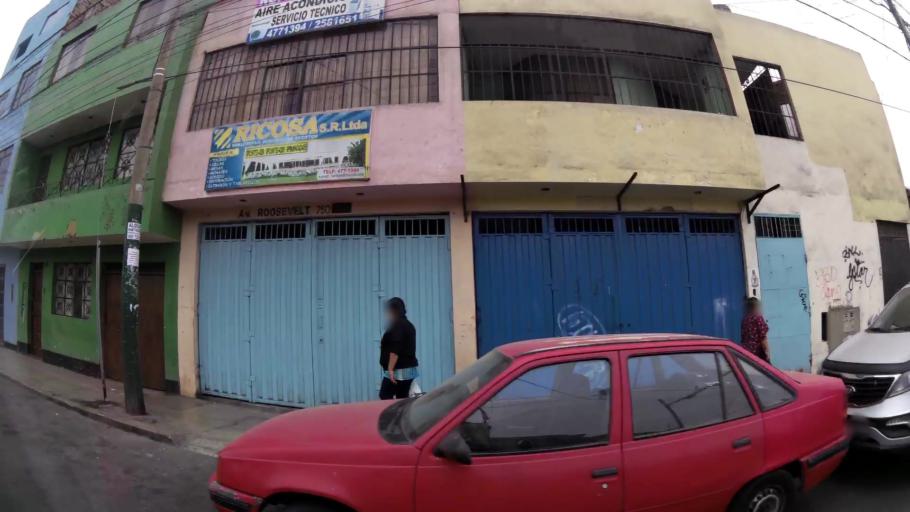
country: PE
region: Lima
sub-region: Lima
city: Surco
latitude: -12.1470
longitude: -77.0127
